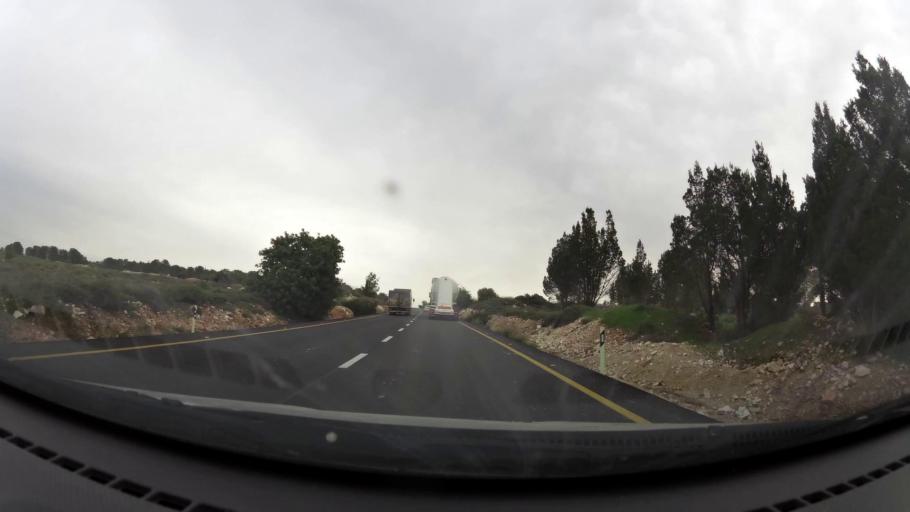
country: PS
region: West Bank
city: Surif
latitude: 31.6754
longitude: 35.0328
